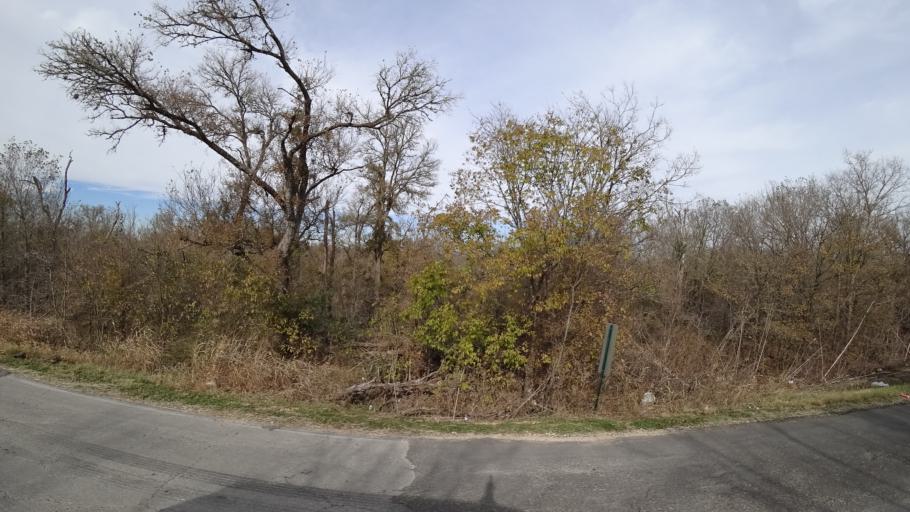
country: US
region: Texas
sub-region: Travis County
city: Garfield
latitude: 30.1295
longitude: -97.6043
